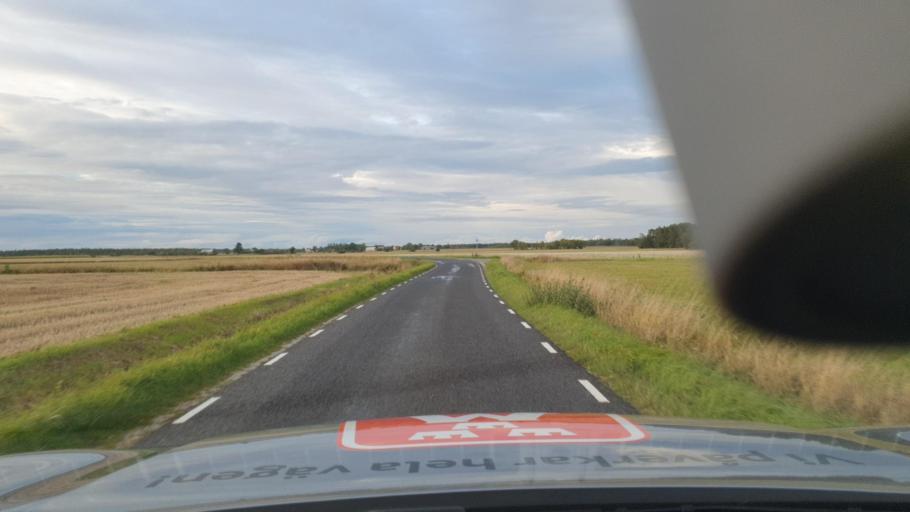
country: SE
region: Gotland
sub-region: Gotland
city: Visby
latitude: 57.6228
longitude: 18.4717
